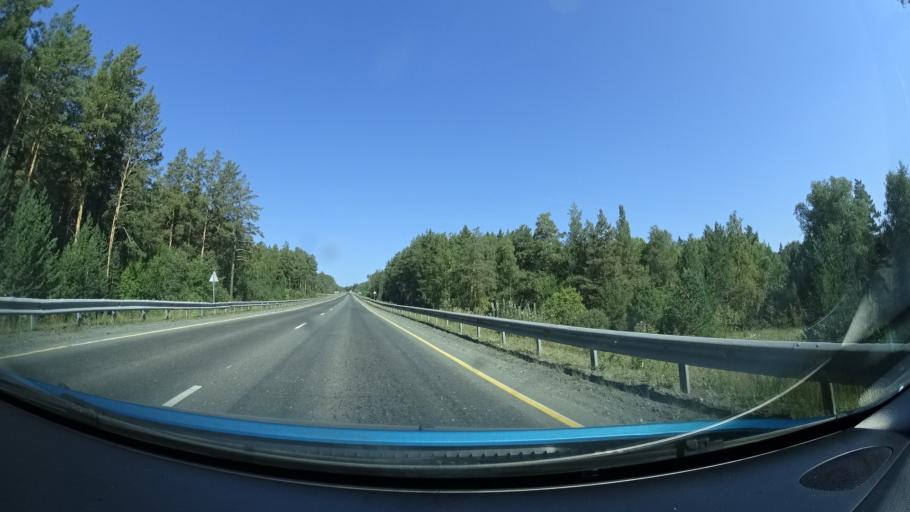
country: RU
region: Bashkortostan
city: Abzakovo
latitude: 53.8780
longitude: 58.5329
